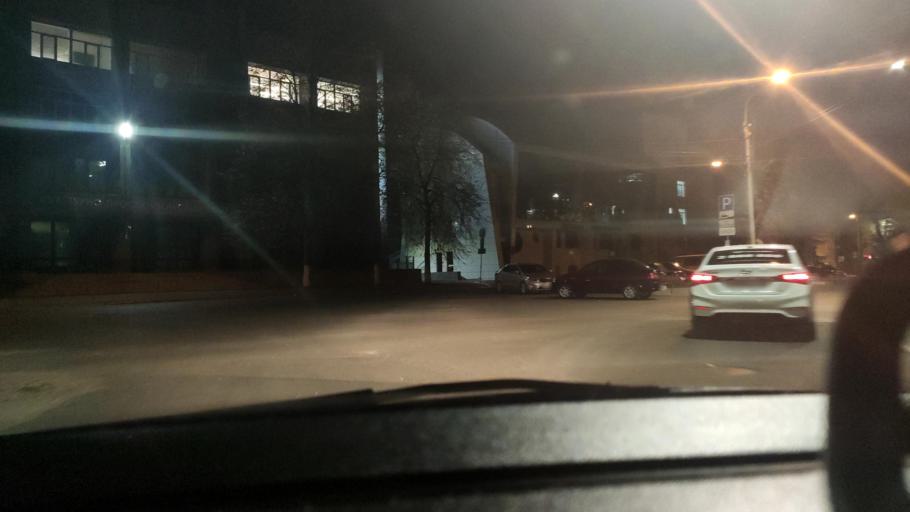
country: RU
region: Voronezj
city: Voronezh
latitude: 51.6530
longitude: 39.1944
